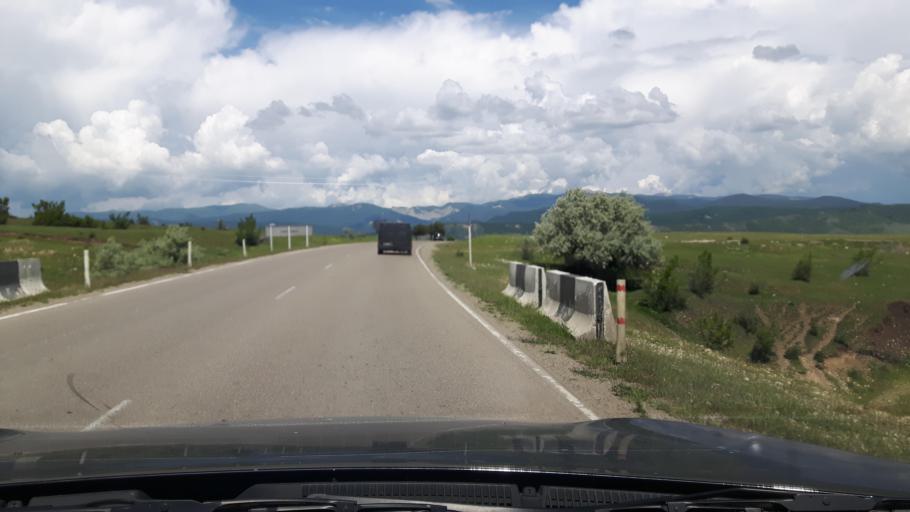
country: GE
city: Didi Lilo
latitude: 41.7509
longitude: 45.1421
